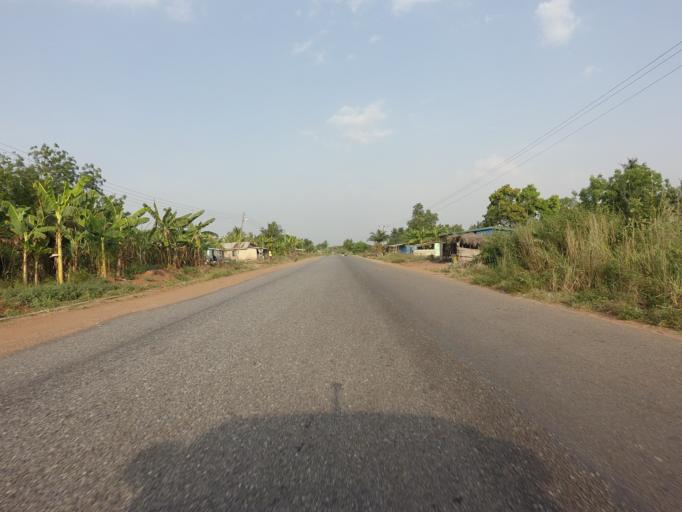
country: GH
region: Volta
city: Ho
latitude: 6.4176
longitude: 0.1758
